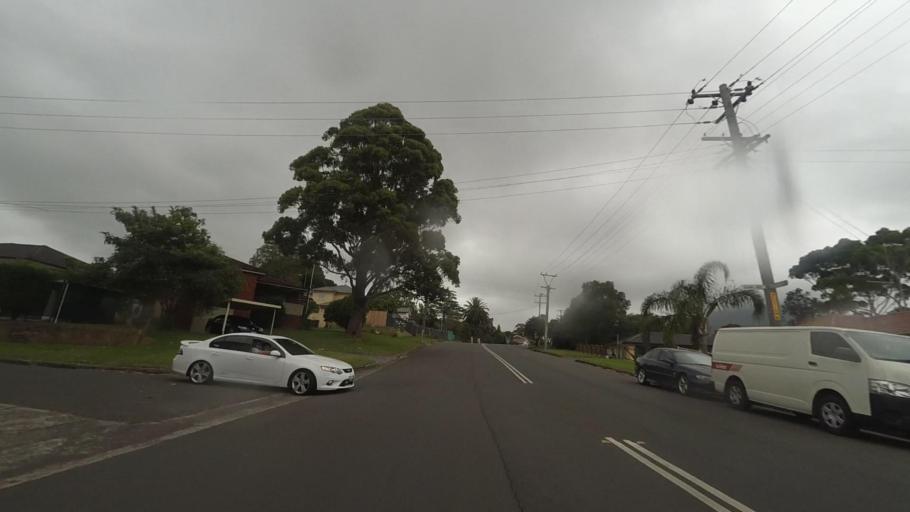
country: AU
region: New South Wales
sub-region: Wollongong
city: Cordeaux Heights
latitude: -34.4510
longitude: 150.8351
